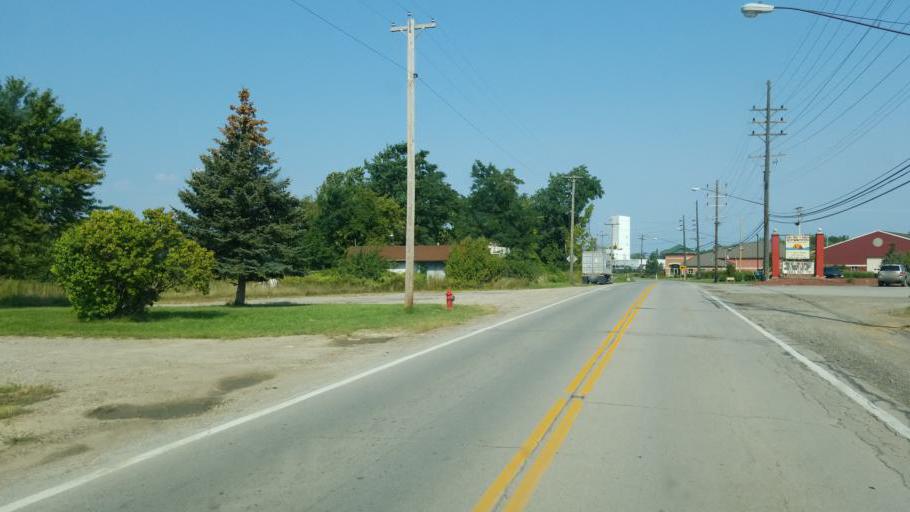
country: US
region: Ohio
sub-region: Lake County
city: Painesville
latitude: 41.7522
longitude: -81.2294
